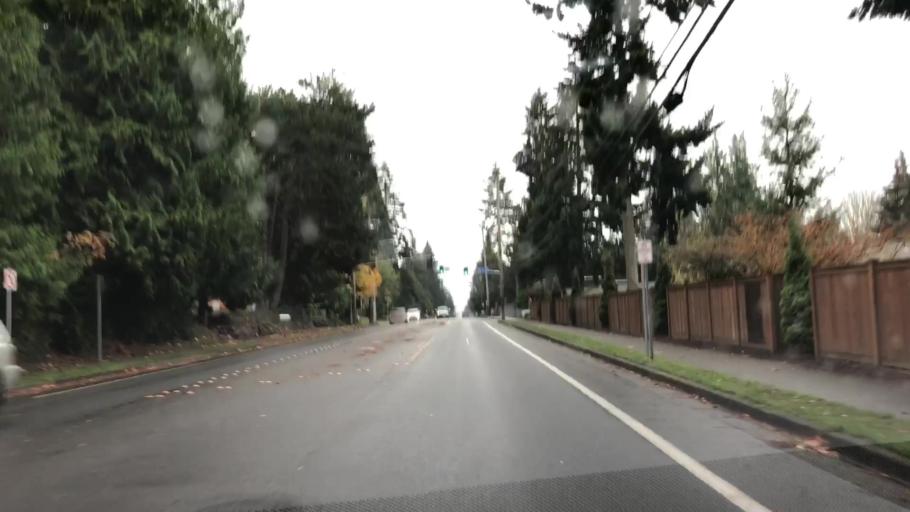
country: US
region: Washington
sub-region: Snohomish County
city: Alderwood Manor
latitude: 47.8400
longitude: -122.2925
